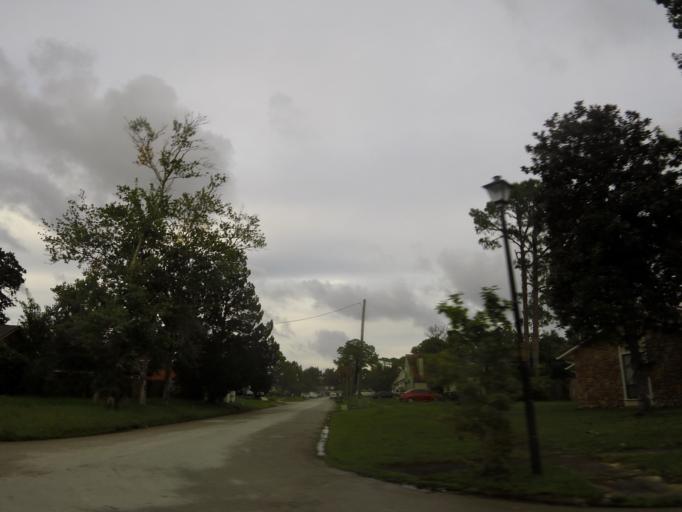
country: US
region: Florida
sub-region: Duval County
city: Neptune Beach
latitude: 30.3020
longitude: -81.5170
